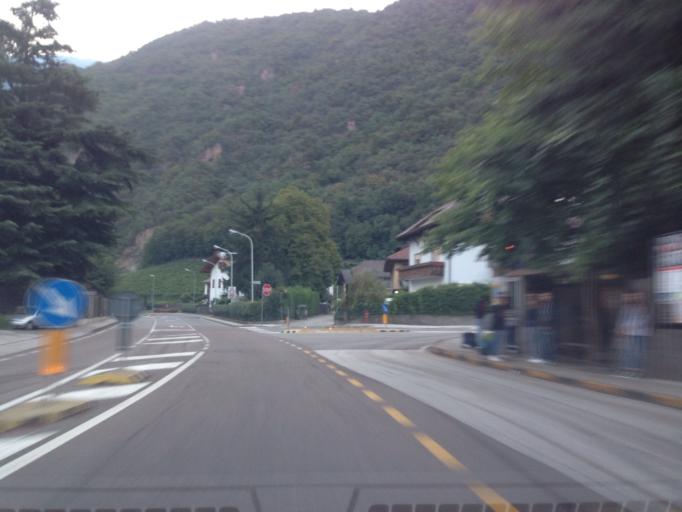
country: IT
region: Trentino-Alto Adige
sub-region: Bolzano
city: Laives
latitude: 46.4294
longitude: 11.3439
